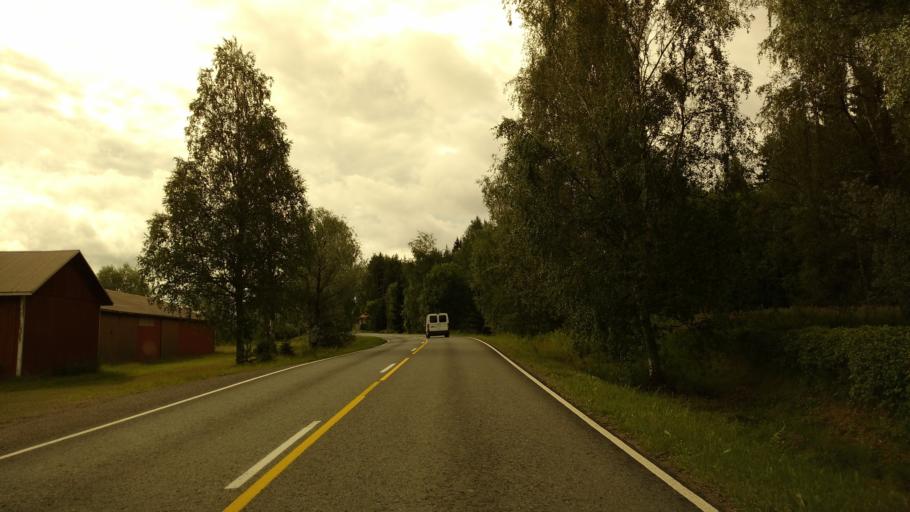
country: FI
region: Varsinais-Suomi
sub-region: Salo
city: Kuusjoki
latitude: 60.5269
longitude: 23.1724
